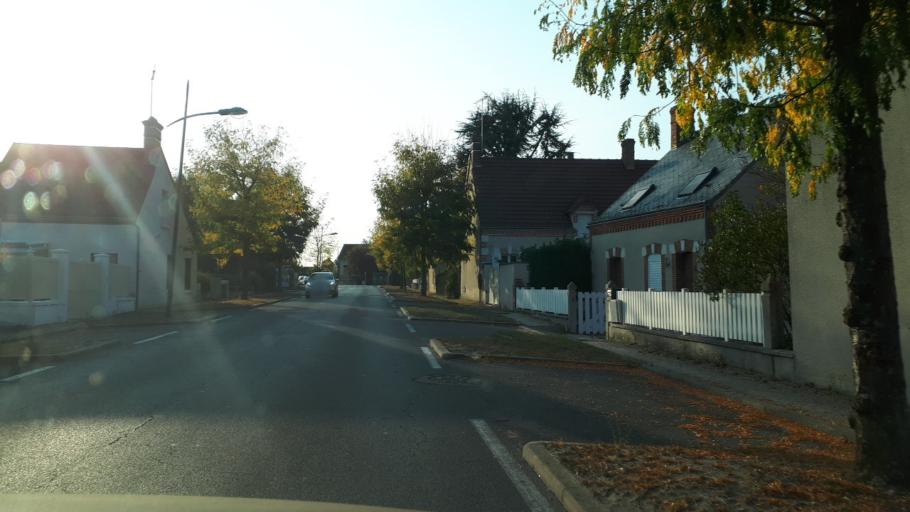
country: FR
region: Centre
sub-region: Departement du Loir-et-Cher
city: Romorantin-Lanthenay
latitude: 47.3659
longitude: 1.7233
